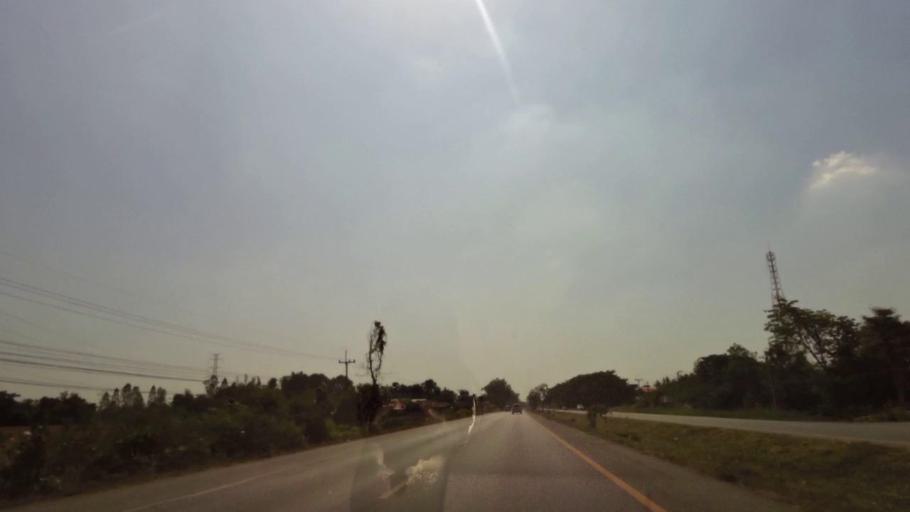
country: TH
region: Phichit
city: Wachira Barami
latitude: 16.3890
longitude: 100.1383
